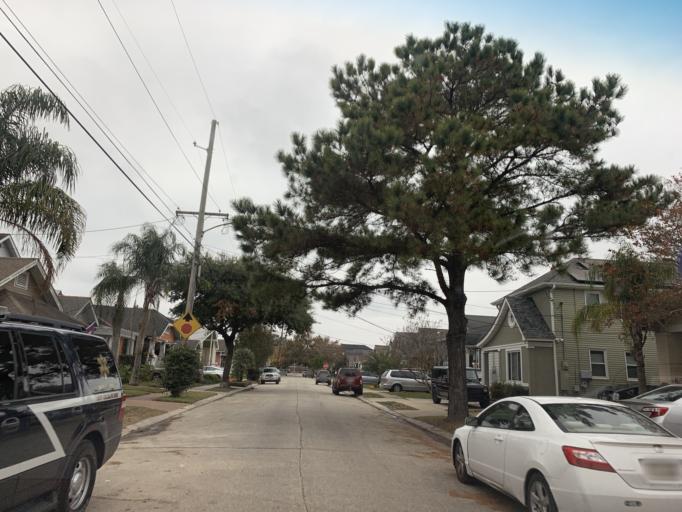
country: US
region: Louisiana
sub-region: Jefferson Parish
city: Metairie
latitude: 29.9905
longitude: -90.1071
